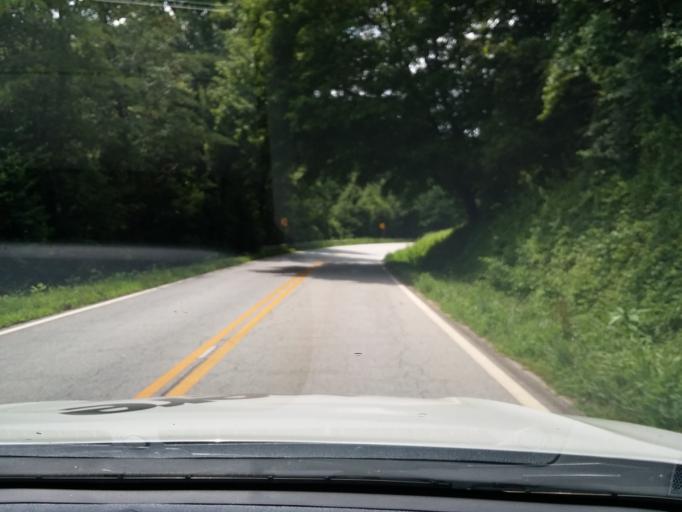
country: US
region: Georgia
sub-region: Rabun County
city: Mountain City
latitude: 34.8905
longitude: -83.3038
